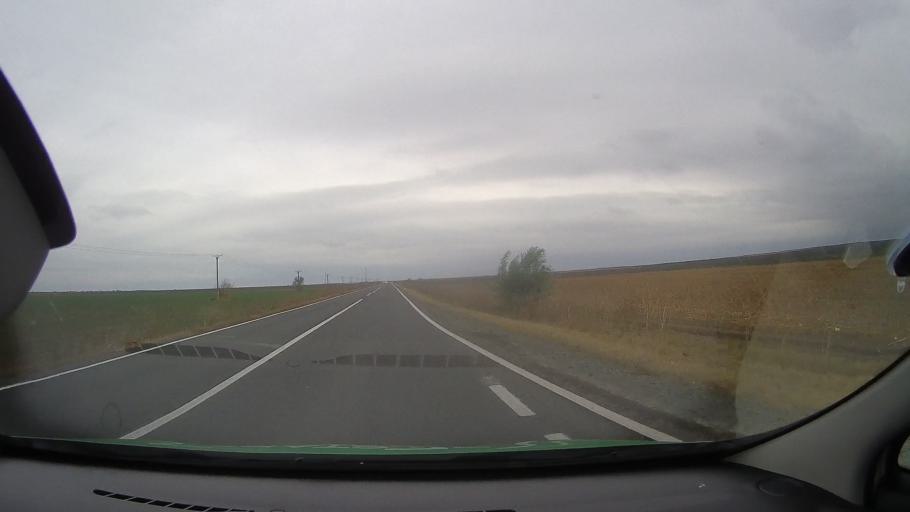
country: RO
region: Constanta
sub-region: Comuna Nicolae Balcescu
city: Nicolae Balcescu
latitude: 44.3799
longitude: 28.4094
